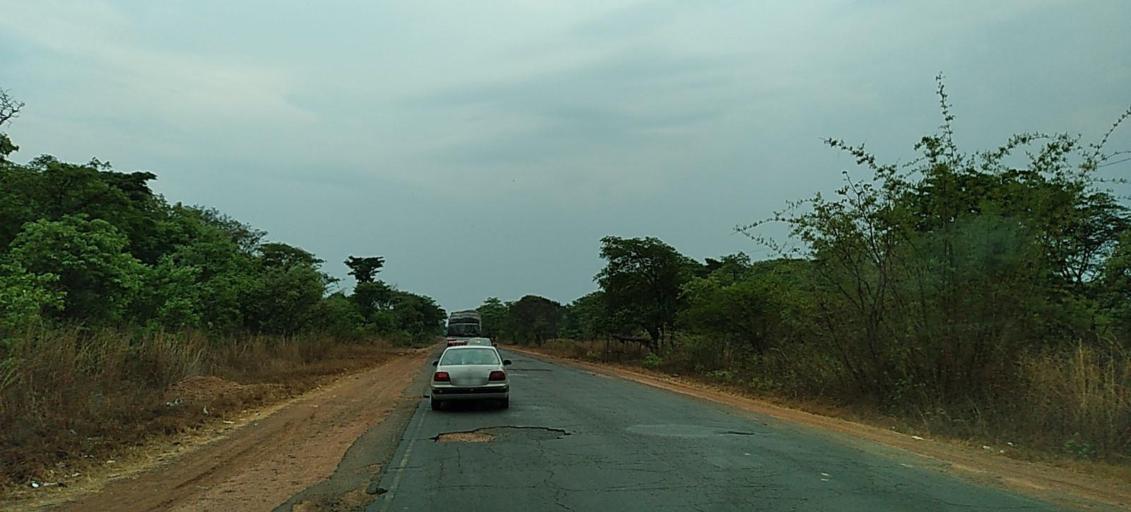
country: ZM
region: Copperbelt
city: Luanshya
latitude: -13.0870
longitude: 28.4371
